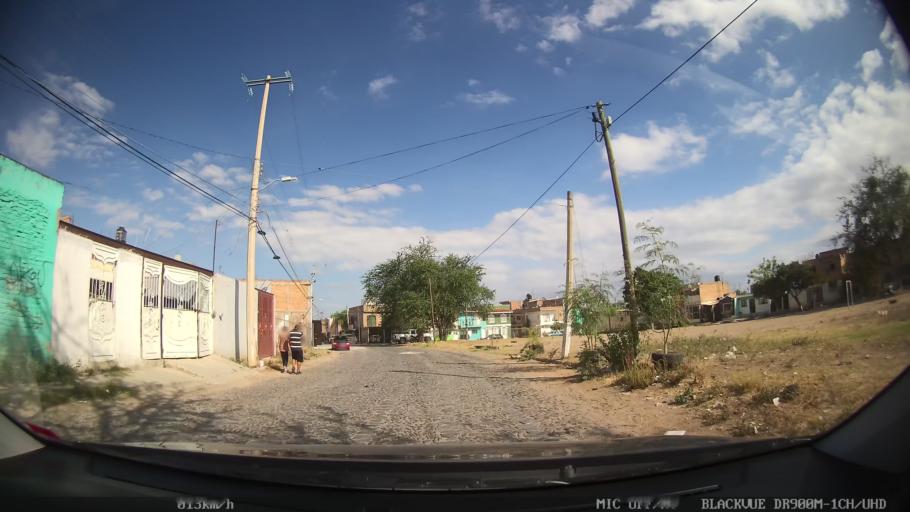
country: MX
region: Jalisco
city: Tonala
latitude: 20.6500
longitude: -103.2498
